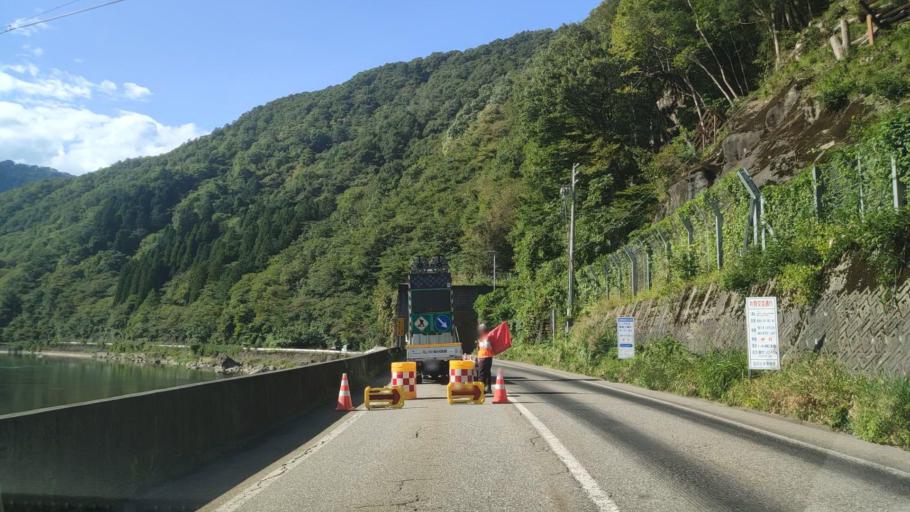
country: JP
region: Gifu
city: Takayama
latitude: 36.2782
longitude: 137.1354
